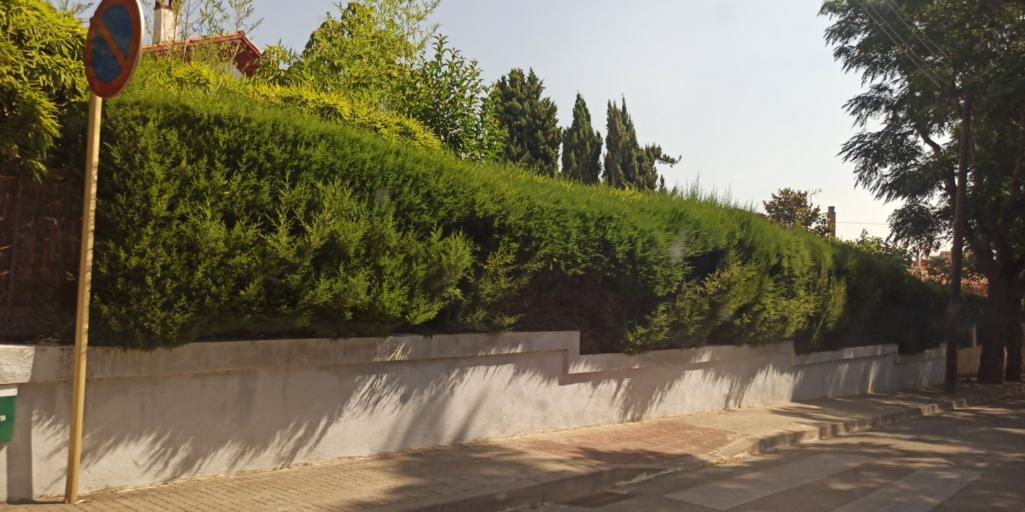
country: ES
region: Catalonia
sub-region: Provincia de Barcelona
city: Cerdanyola del Valles
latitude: 41.4883
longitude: 2.1376
